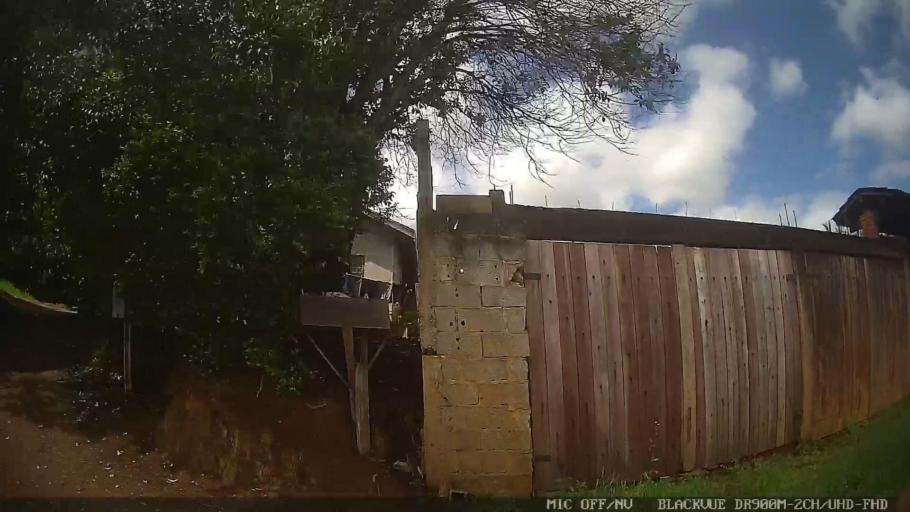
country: BR
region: Sao Paulo
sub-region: Amparo
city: Amparo
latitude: -22.8637
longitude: -46.6995
